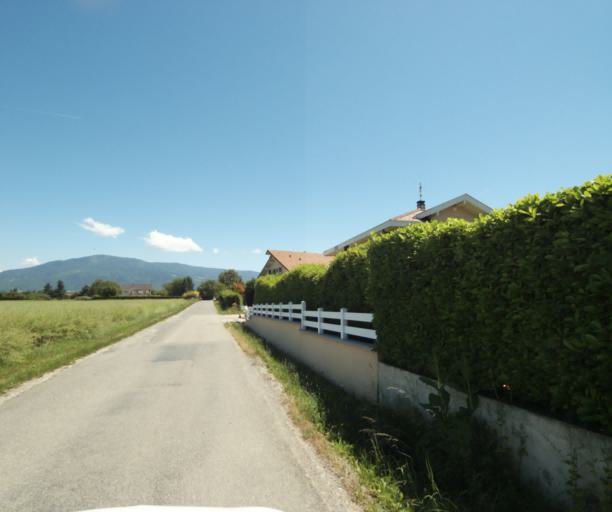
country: FR
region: Rhone-Alpes
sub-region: Departement de la Haute-Savoie
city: Veigy-Foncenex
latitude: 46.2620
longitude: 6.2577
